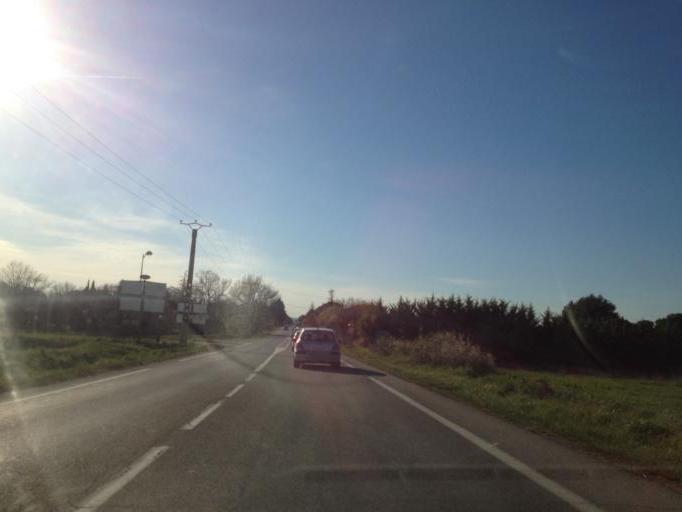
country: FR
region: Provence-Alpes-Cote d'Azur
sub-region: Departement des Bouches-du-Rhone
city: Saint-Cannat
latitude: 43.6161
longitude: 5.3160
